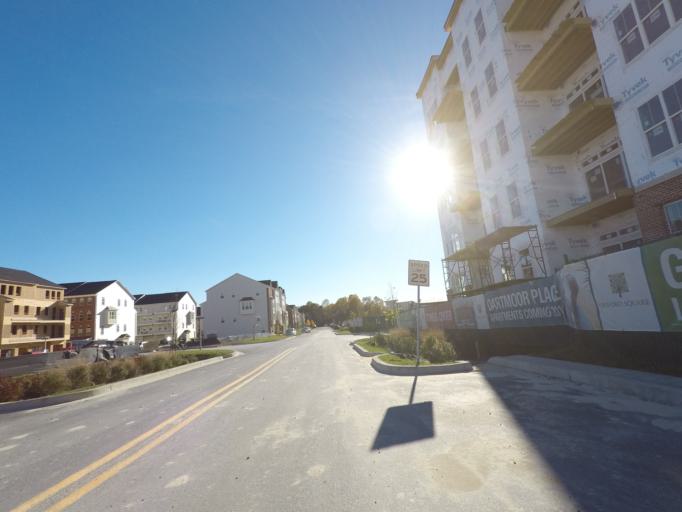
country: US
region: Maryland
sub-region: Howard County
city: Hanover
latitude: 39.1853
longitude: -76.7397
